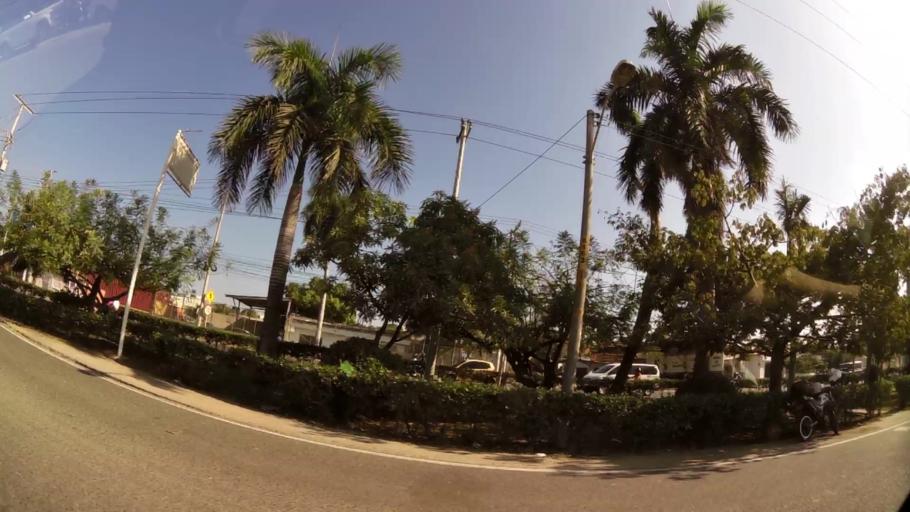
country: CO
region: Bolivar
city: Cartagena
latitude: 10.3876
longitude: -75.5121
